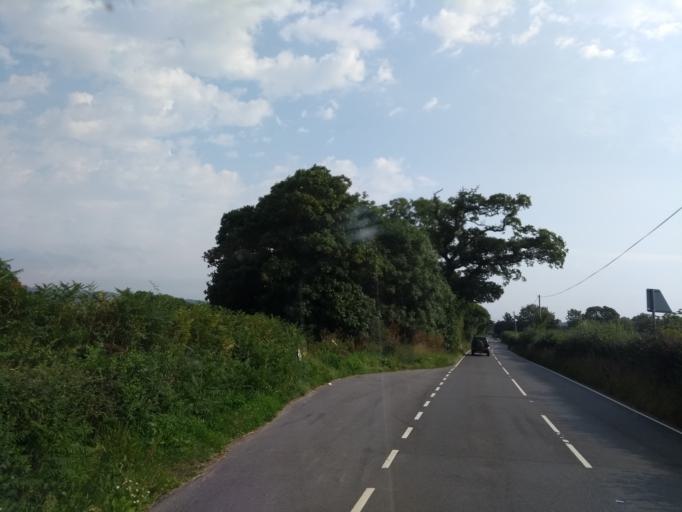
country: GB
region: England
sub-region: Devon
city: Axminster
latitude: 50.7644
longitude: -3.0115
